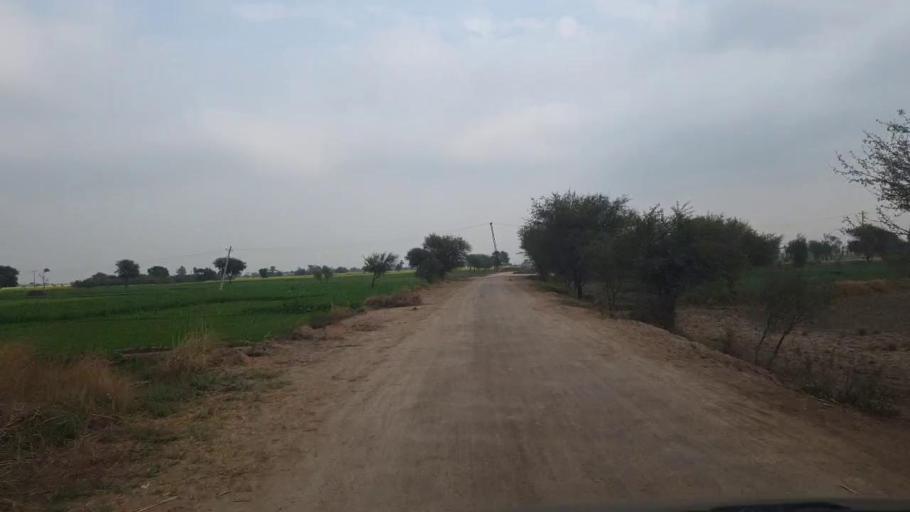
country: PK
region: Sindh
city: Shahdadpur
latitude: 25.8902
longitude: 68.7039
